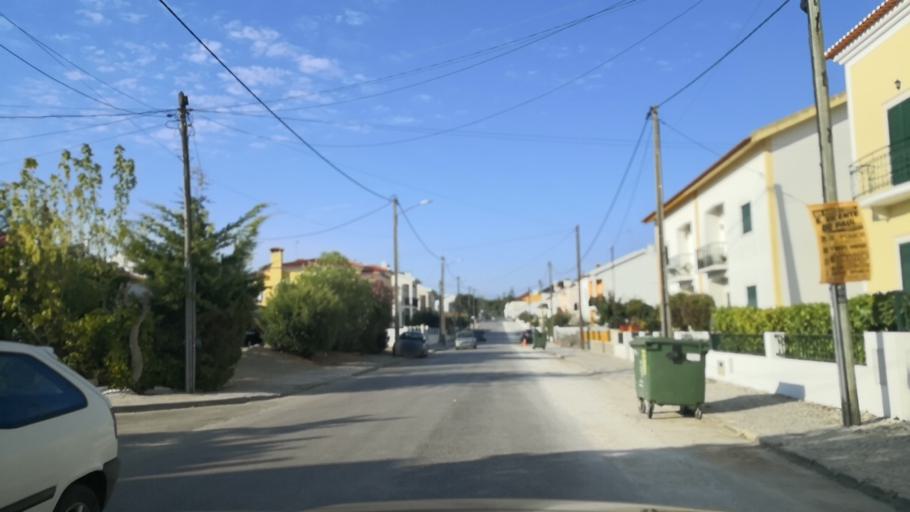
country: PT
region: Santarem
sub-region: Santarem
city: Santarem
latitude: 39.2526
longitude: -8.6834
